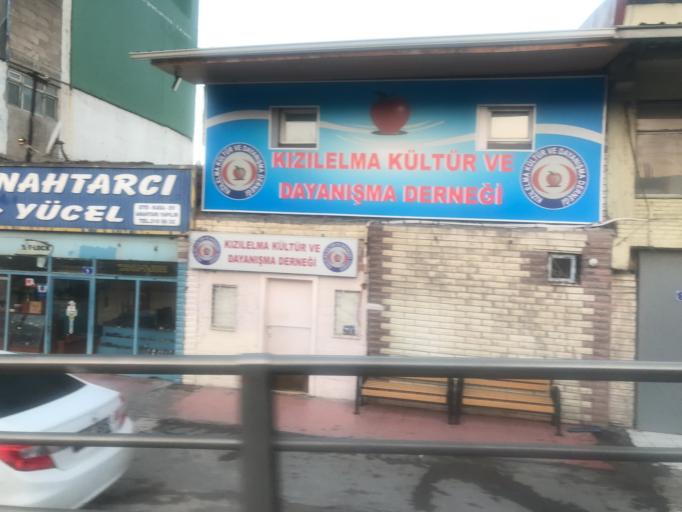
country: TR
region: Ankara
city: Ankara
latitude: 39.9500
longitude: 32.8575
